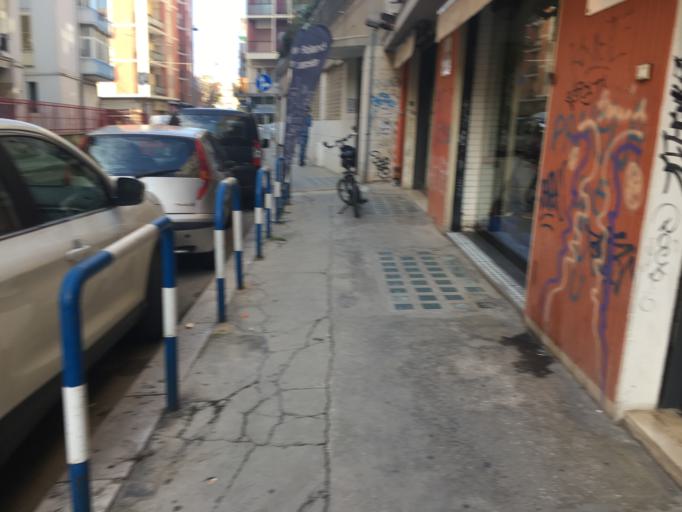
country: IT
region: Apulia
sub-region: Provincia di Bari
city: Bari
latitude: 41.1128
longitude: 16.8713
